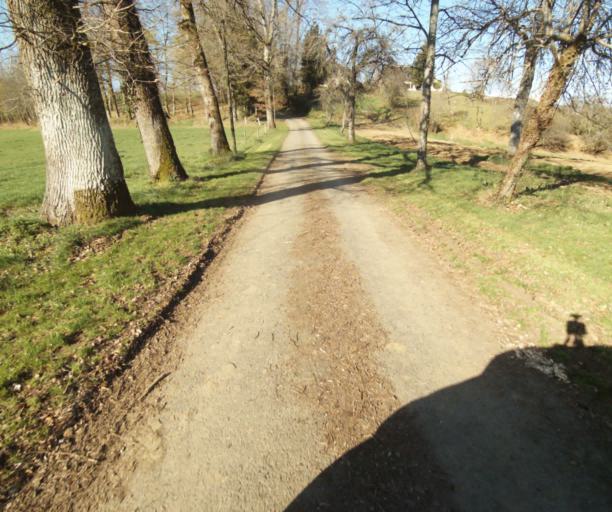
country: FR
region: Limousin
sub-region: Departement de la Correze
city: Seilhac
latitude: 45.3737
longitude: 1.7515
